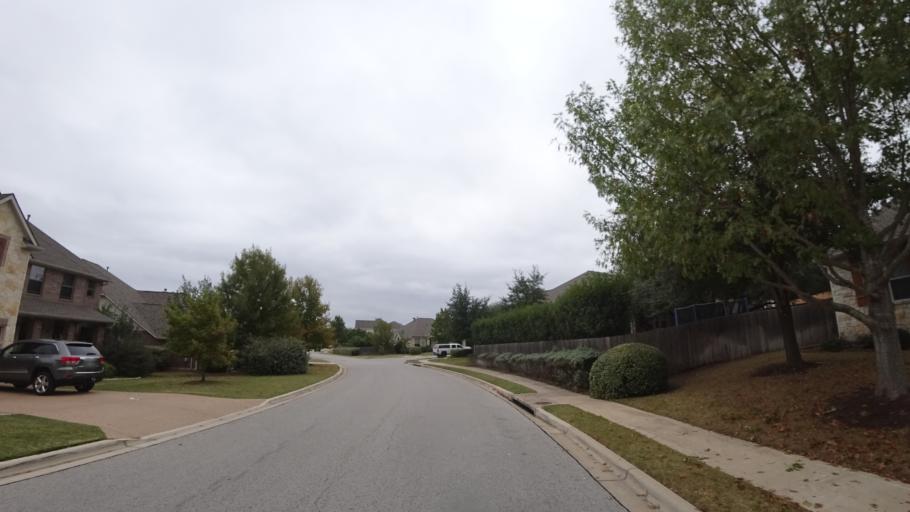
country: US
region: Texas
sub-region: Travis County
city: Bee Cave
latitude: 30.3554
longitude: -97.9041
